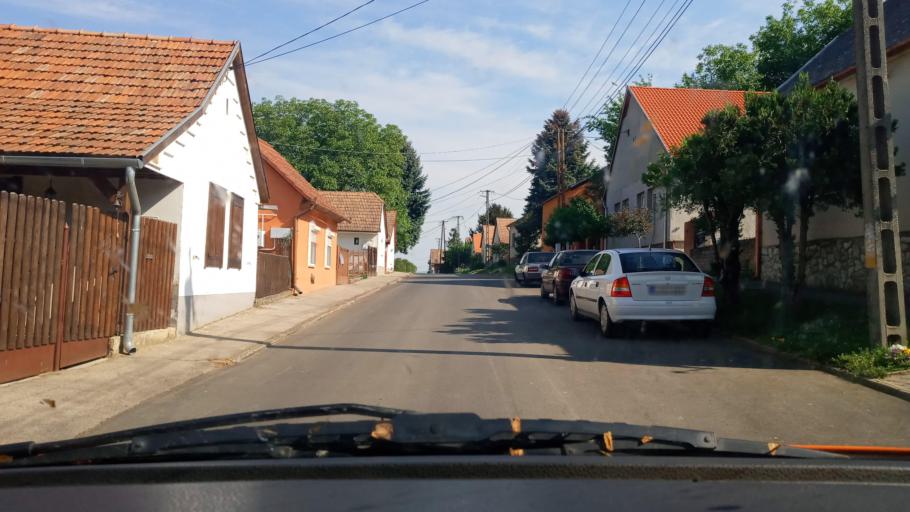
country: HU
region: Baranya
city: Kozarmisleny
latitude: 46.0113
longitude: 18.2769
